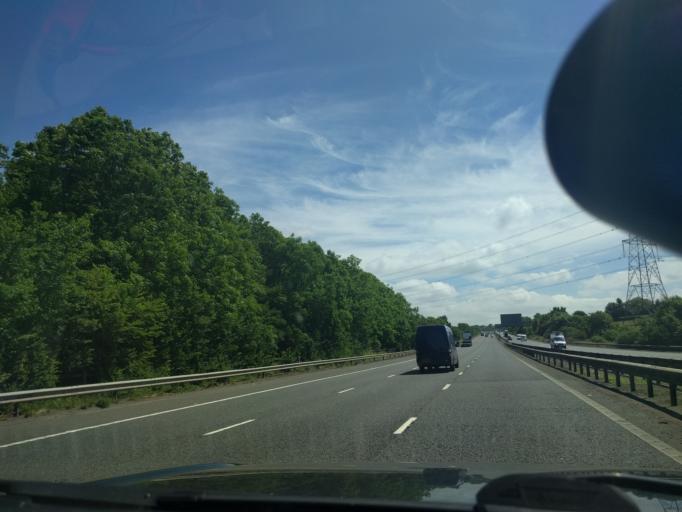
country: GB
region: England
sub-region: South Gloucestershire
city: Almondsbury
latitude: 51.5694
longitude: -2.5770
